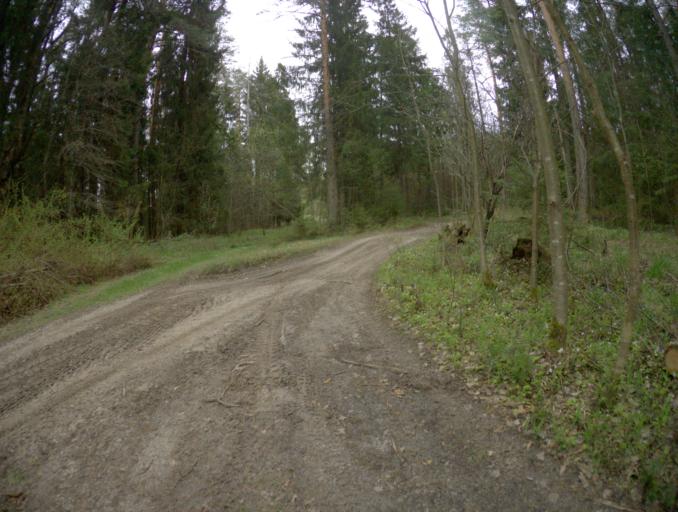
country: RU
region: Vladimir
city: Golovino
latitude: 55.9001
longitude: 40.4340
